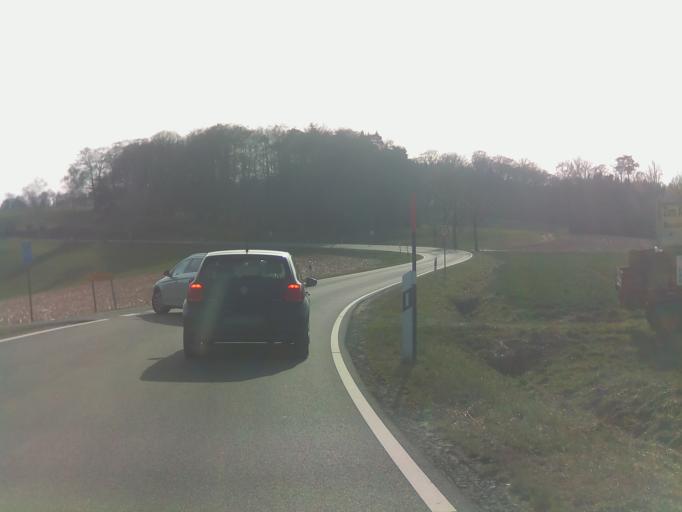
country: DE
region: Hesse
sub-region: Regierungsbezirk Darmstadt
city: Brensbach
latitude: 49.7323
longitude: 8.9186
